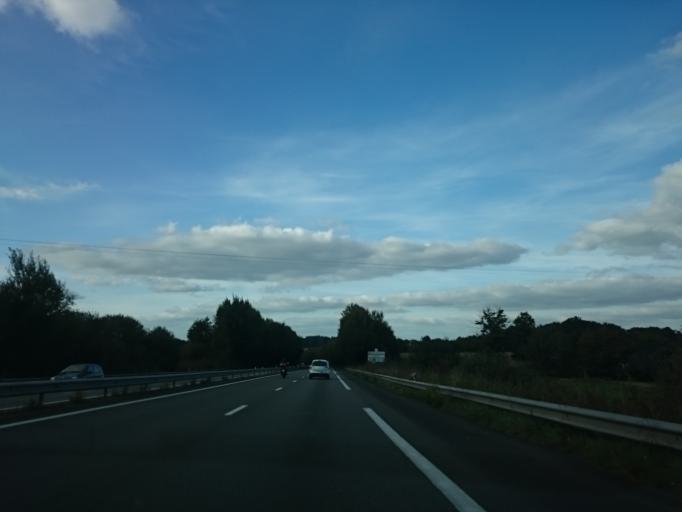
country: FR
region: Pays de la Loire
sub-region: Departement de la Loire-Atlantique
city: Treillieres
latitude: 47.3164
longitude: -1.6428
